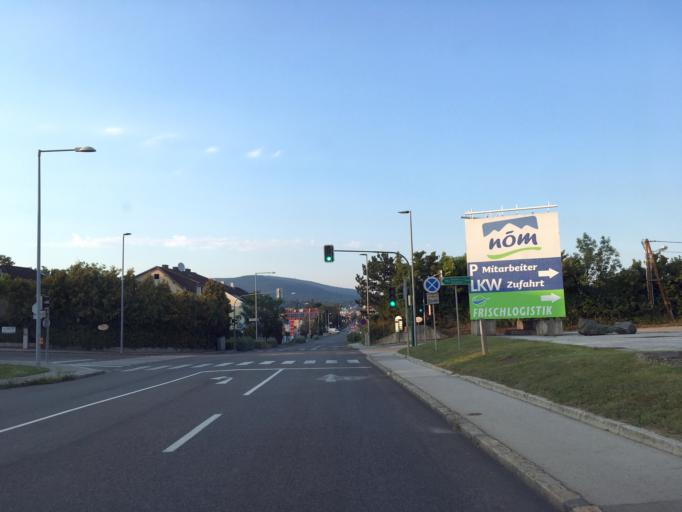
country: AT
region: Lower Austria
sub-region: Politischer Bezirk Baden
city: Baden
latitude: 47.9938
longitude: 16.2261
